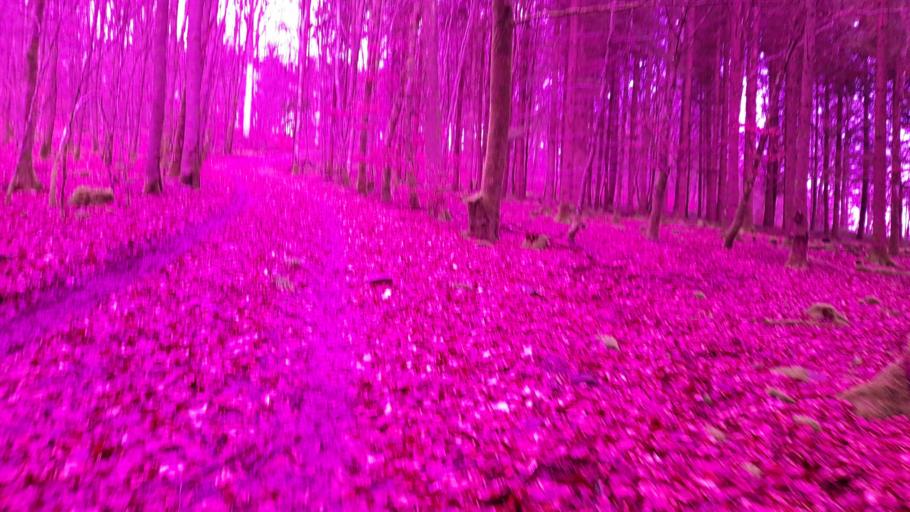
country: DE
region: Rheinland-Pfalz
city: Dasburg
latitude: 50.0677
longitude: 6.1195
